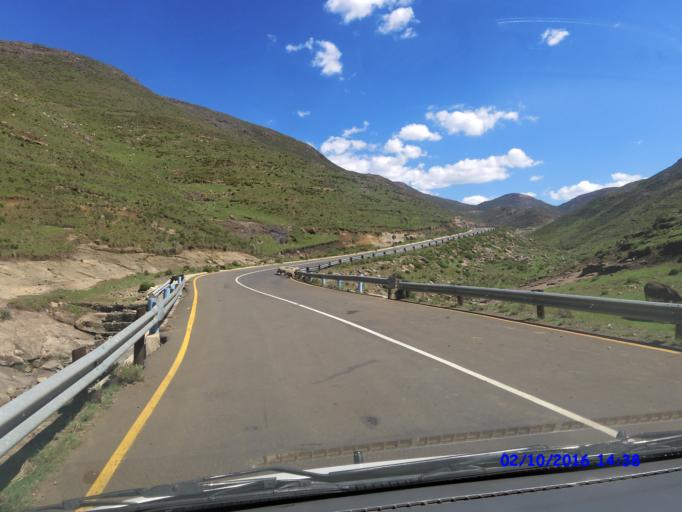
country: LS
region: Maseru
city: Nako
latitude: -29.5095
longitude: 28.0633
